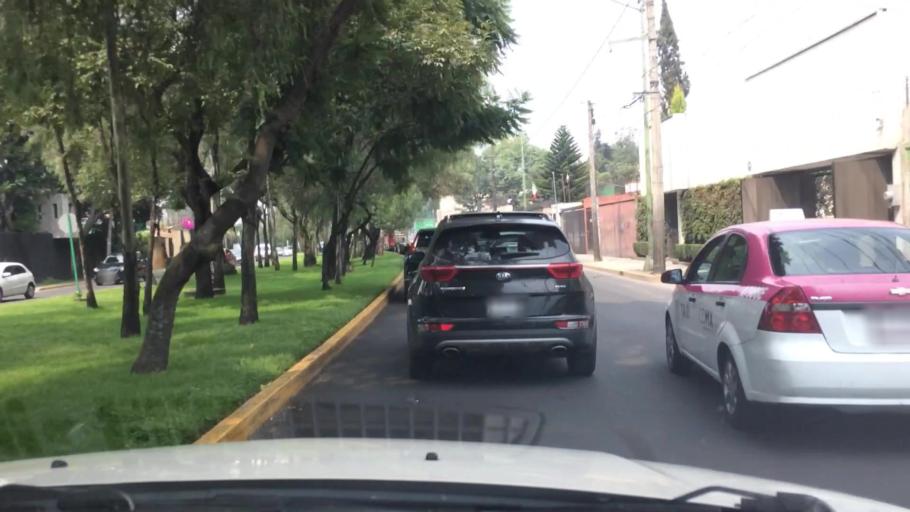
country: MX
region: Mexico City
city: Magdalena Contreras
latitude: 19.3105
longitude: -99.2034
